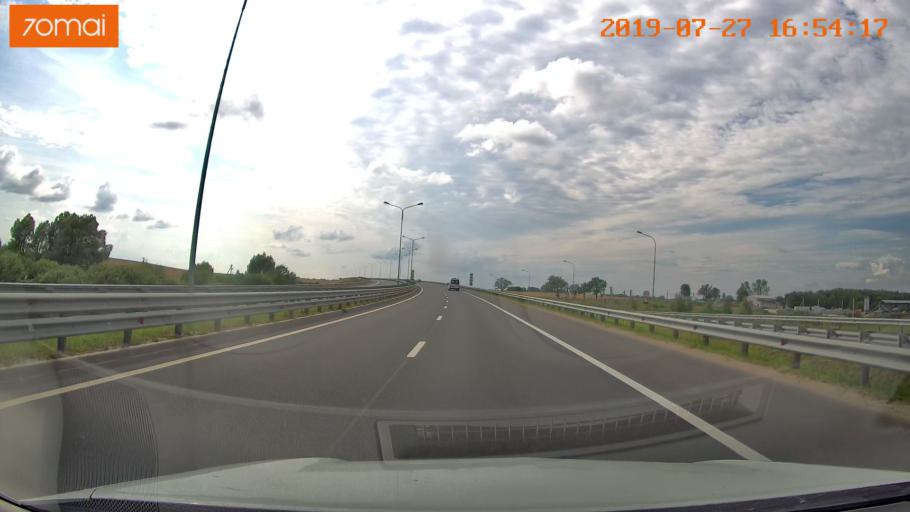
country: RU
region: Kaliningrad
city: Bol'shoe Isakovo
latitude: 54.6937
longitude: 20.8098
